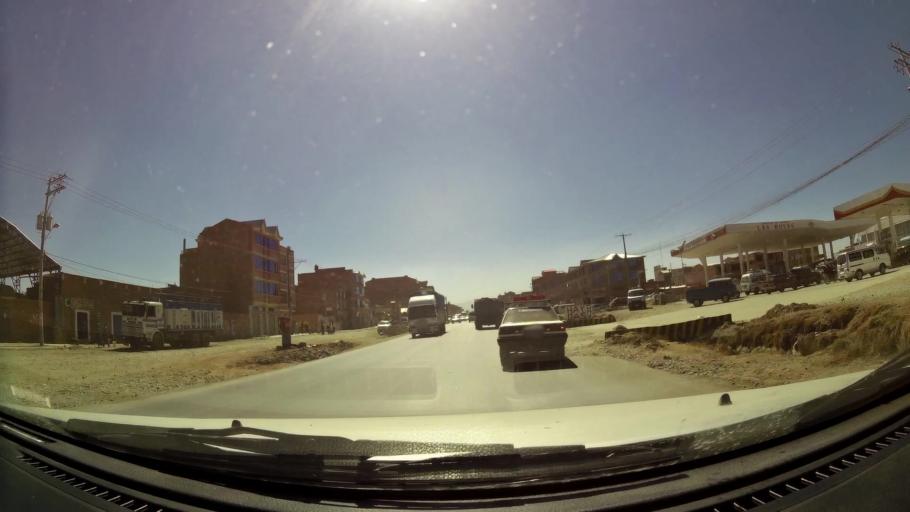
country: BO
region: La Paz
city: La Paz
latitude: -16.5474
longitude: -68.2025
